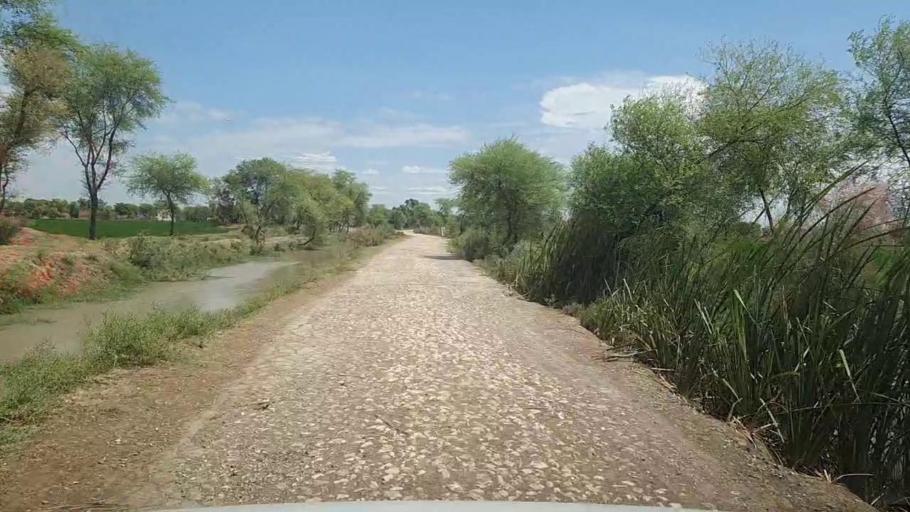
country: PK
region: Sindh
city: Kandhkot
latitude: 28.3413
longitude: 69.2393
